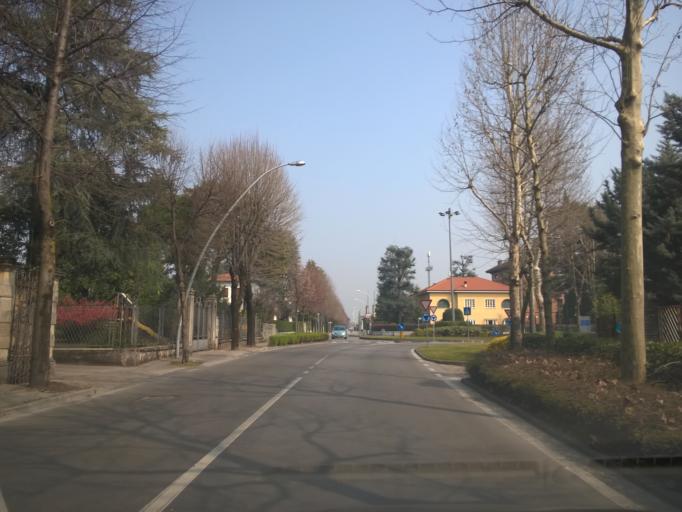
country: IT
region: Veneto
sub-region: Provincia di Vicenza
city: Thiene
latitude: 45.7100
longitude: 11.4812
